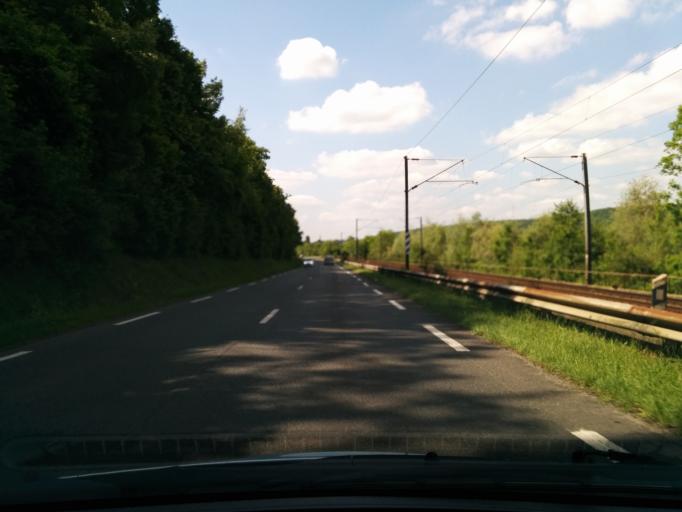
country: FR
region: Ile-de-France
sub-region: Departement des Yvelines
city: Limetz-Villez
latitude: 49.0696
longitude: 1.5176
